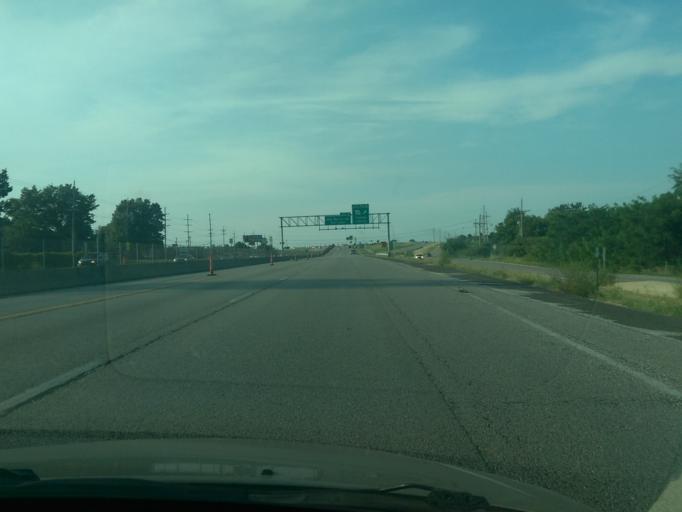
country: US
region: Missouri
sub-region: Platte County
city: Weatherby Lake
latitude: 39.2390
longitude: -94.6583
